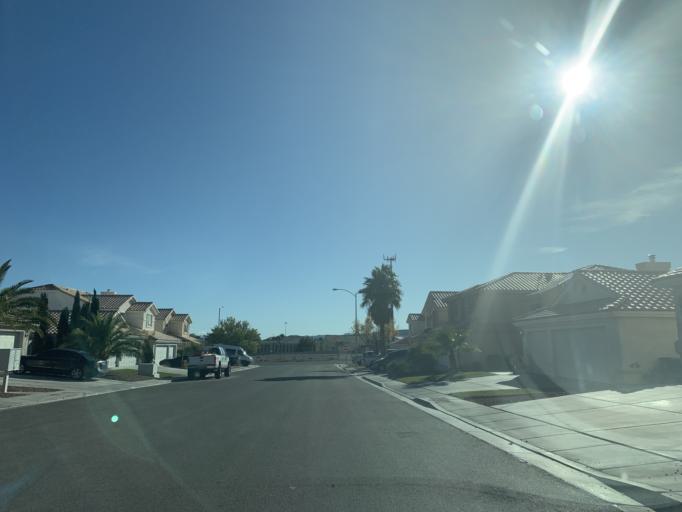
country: US
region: Nevada
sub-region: Clark County
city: Summerlin South
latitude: 36.1215
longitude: -115.3076
